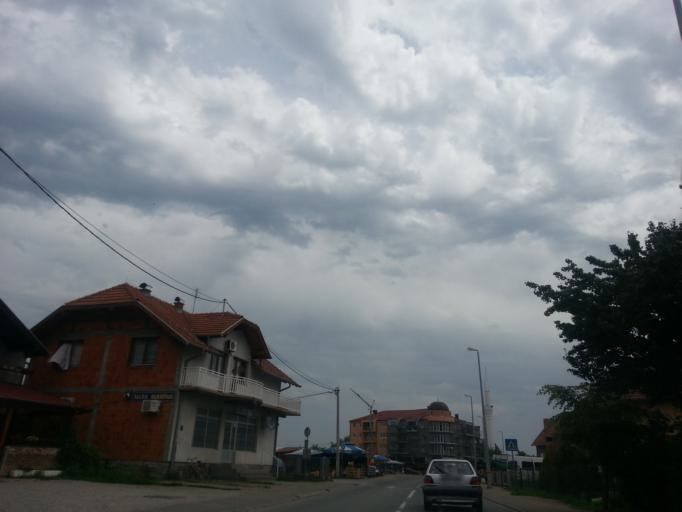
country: BA
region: Brcko
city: Brcko
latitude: 44.8710
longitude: 18.7960
